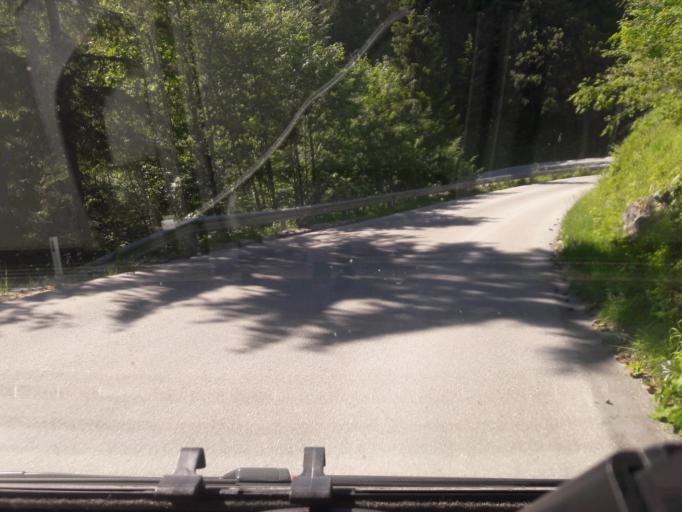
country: AT
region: Styria
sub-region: Politischer Bezirk Liezen
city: Tauplitz
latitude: 47.5735
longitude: 13.9639
